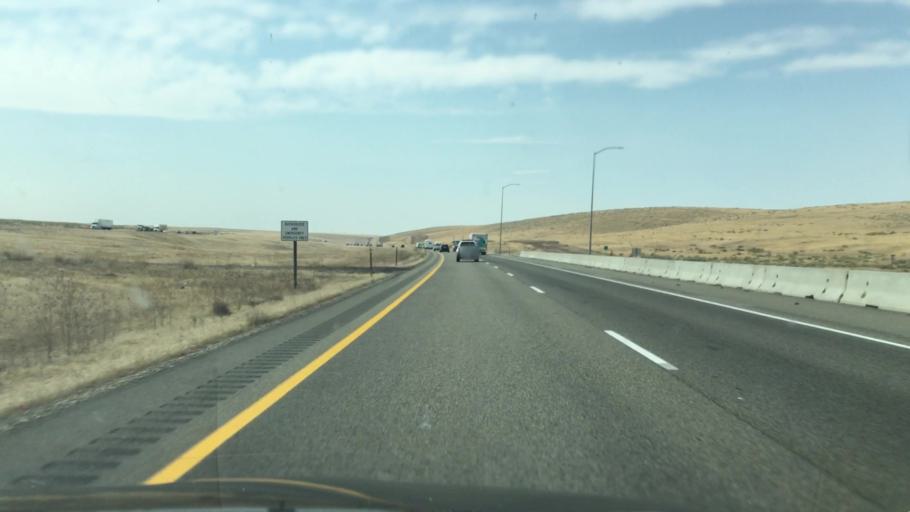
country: US
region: Idaho
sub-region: Ada County
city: Boise
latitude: 43.4796
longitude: -116.1073
